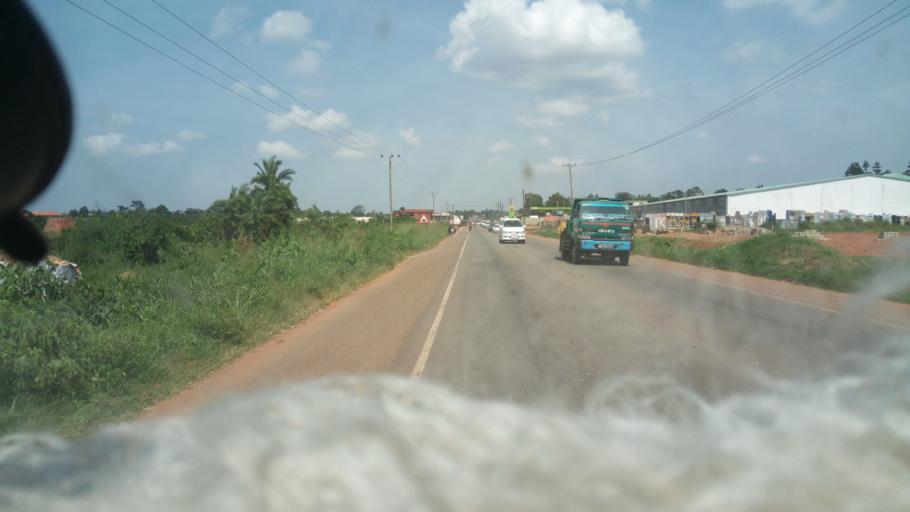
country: UG
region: Central Region
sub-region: Mukono District
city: Mukono
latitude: 0.3535
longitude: 32.7866
